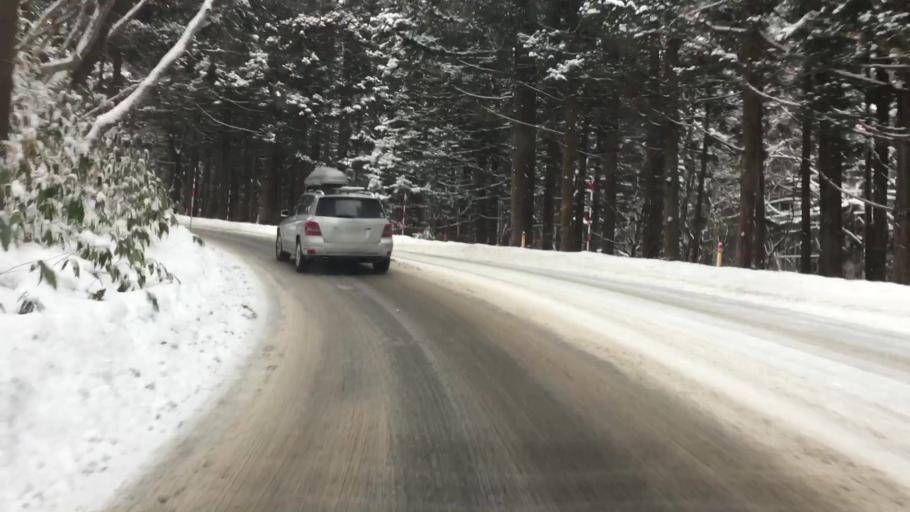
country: JP
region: Tochigi
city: Yaita
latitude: 36.9565
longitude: 139.7780
